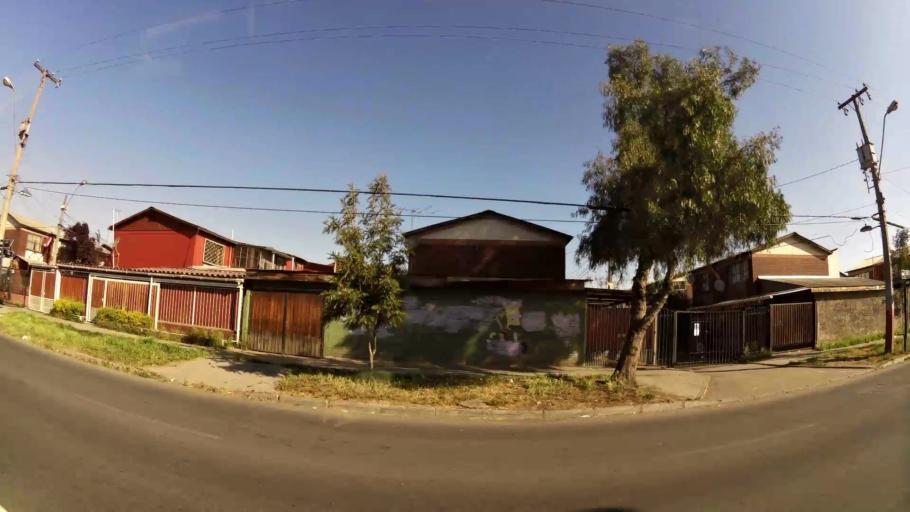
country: CL
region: Santiago Metropolitan
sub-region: Provincia de Santiago
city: La Pintana
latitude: -33.5465
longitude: -70.6202
